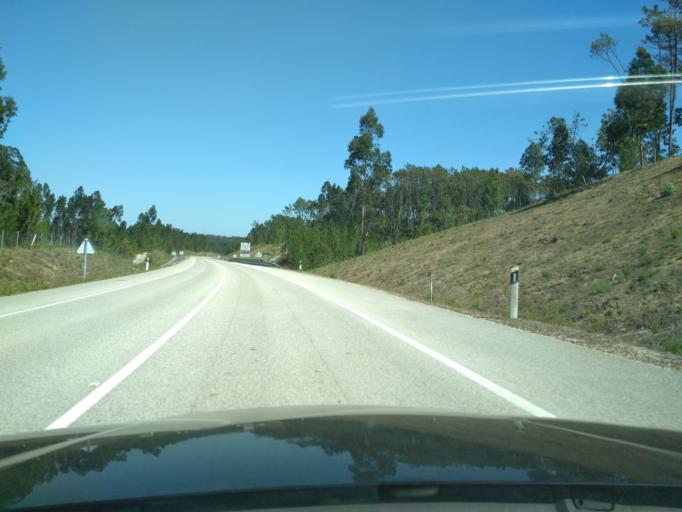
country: PT
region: Leiria
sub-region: Pombal
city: Lourical
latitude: 39.9863
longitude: -8.7496
